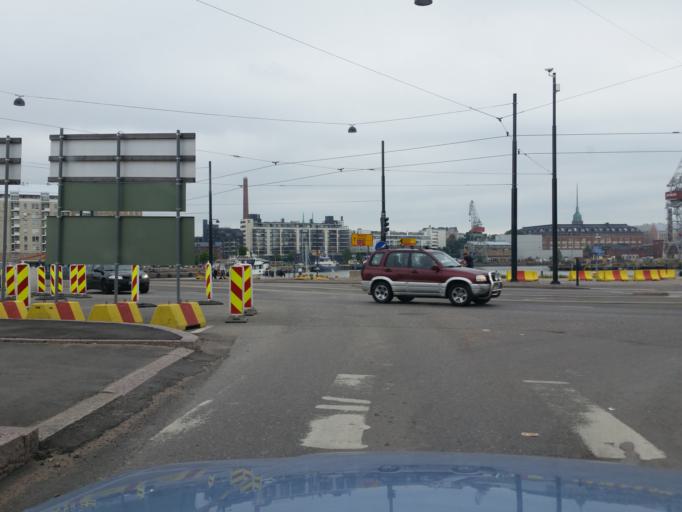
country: FI
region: Uusimaa
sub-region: Helsinki
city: Helsinki
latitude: 60.1602
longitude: 24.9209
